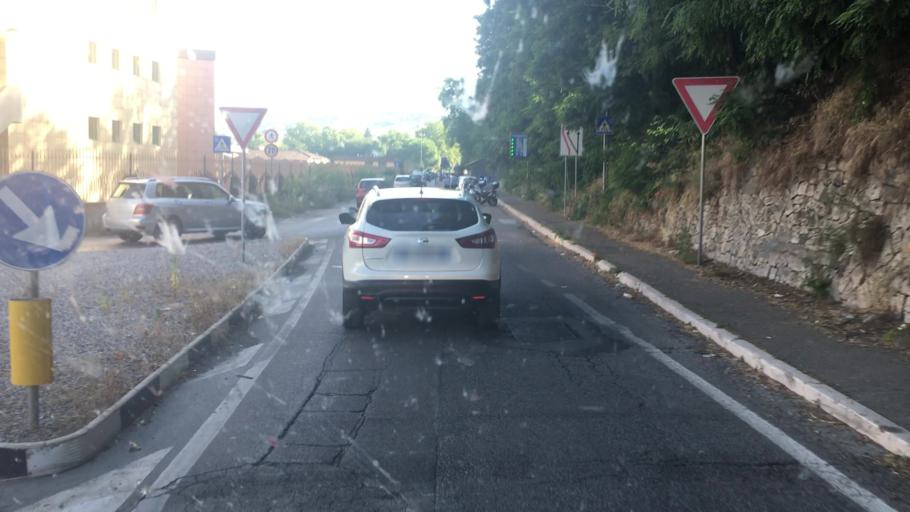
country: IT
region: Basilicate
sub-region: Provincia di Potenza
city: Potenza
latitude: 40.6305
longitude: 15.8093
